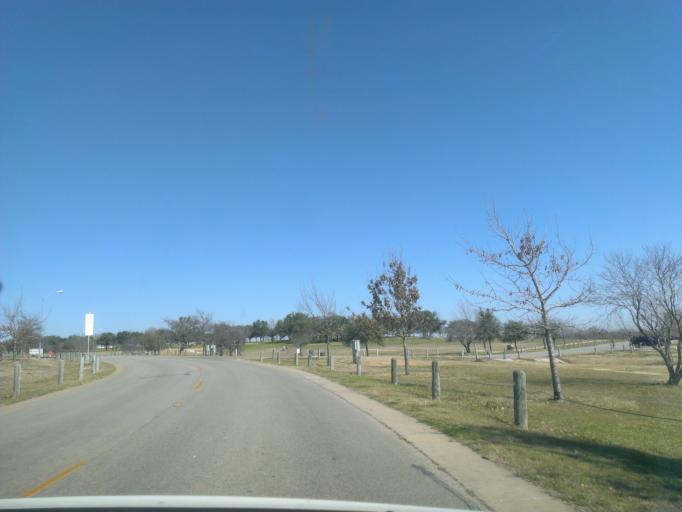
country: US
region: Texas
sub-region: Williamson County
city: Round Rock
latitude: 30.5337
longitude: -97.6288
